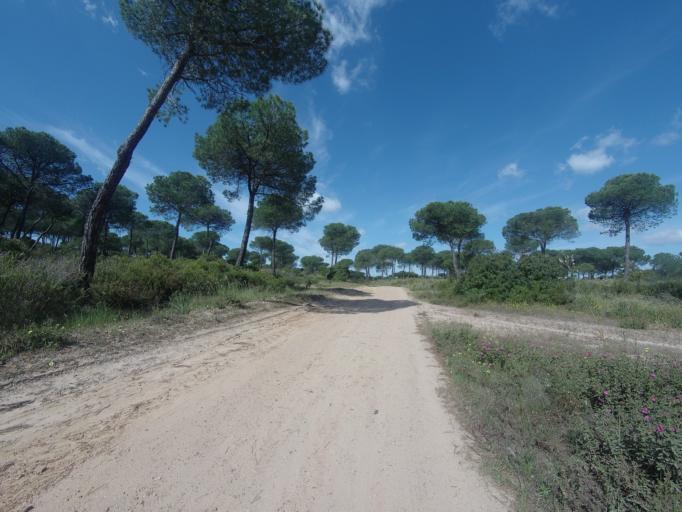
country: ES
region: Andalusia
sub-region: Provincia de Huelva
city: Aljaraque
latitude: 37.2360
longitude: -7.0570
